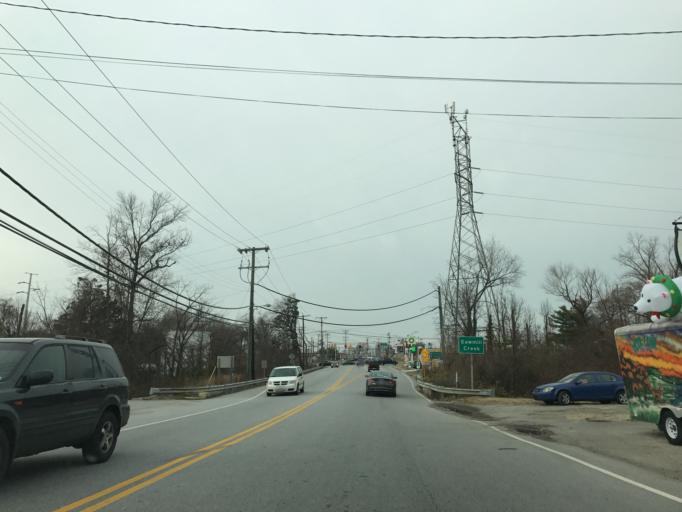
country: US
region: Maryland
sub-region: Anne Arundel County
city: Glen Burnie
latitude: 39.1695
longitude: -76.6294
